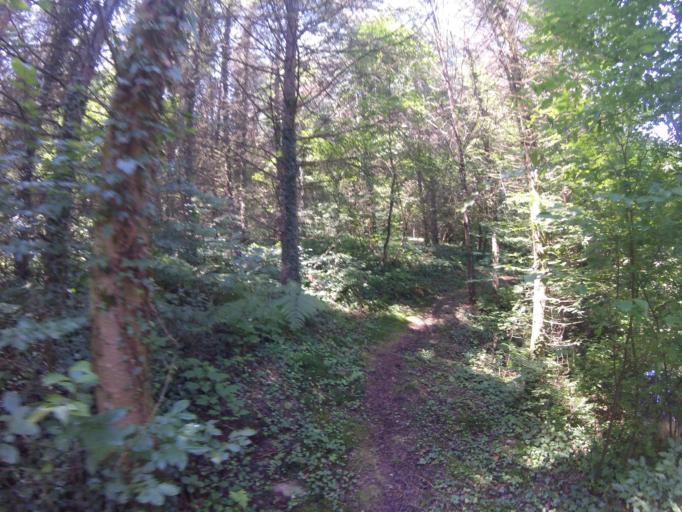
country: HU
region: Zala
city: Letenye
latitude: 46.5057
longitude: 16.6970
